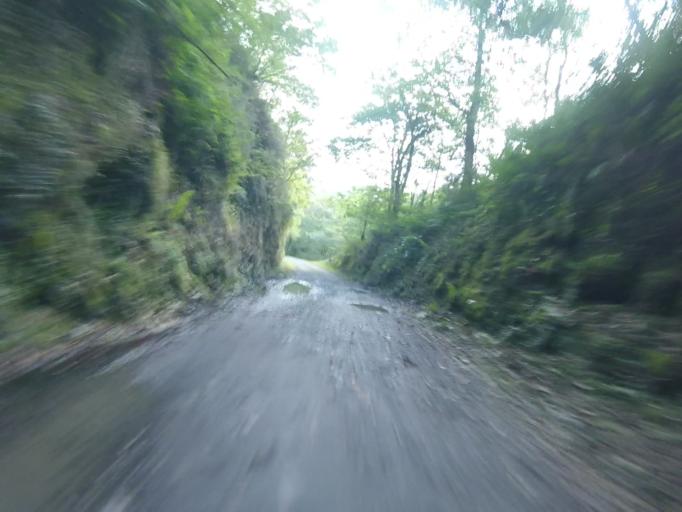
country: ES
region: Basque Country
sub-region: Provincia de Guipuzcoa
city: Berastegui
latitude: 43.1486
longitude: -1.9614
